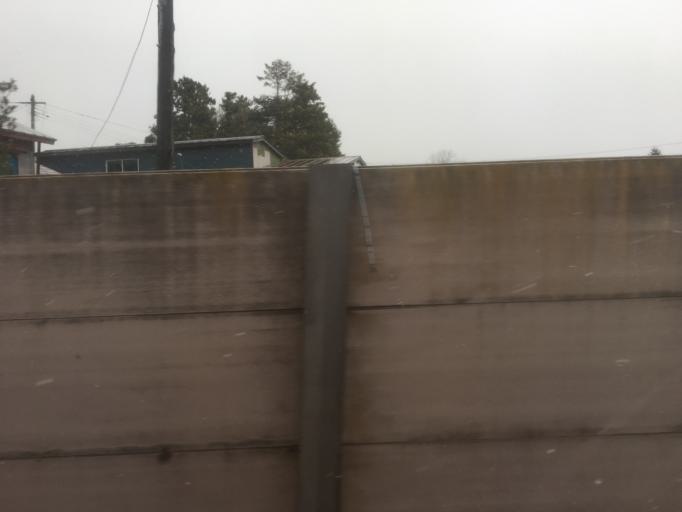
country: JP
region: Aomori
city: Aomori Shi
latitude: 40.9165
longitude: 140.6663
